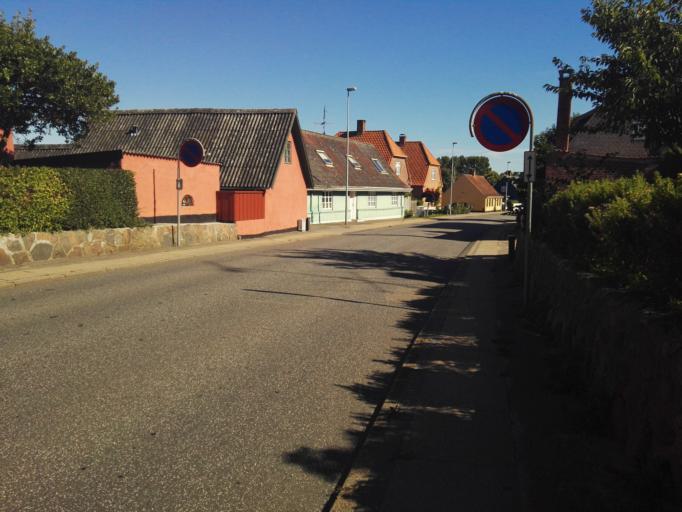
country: DK
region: Zealand
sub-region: Odsherred Kommune
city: Nykobing Sjaelland
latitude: 55.9255
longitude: 11.6729
